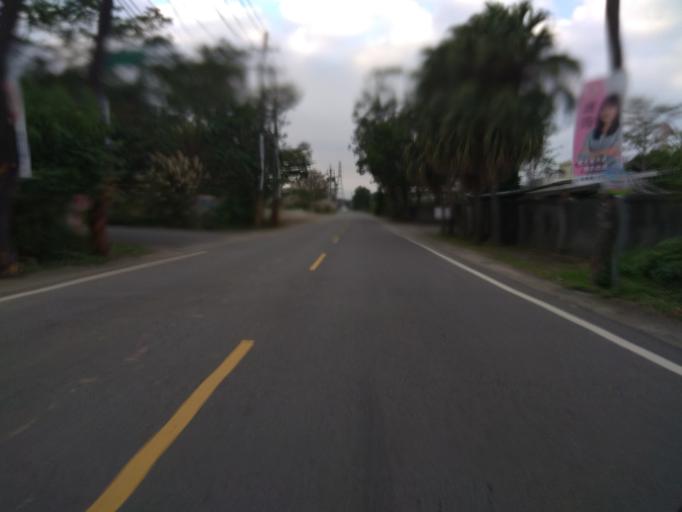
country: TW
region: Taiwan
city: Daxi
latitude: 24.8399
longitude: 121.2061
